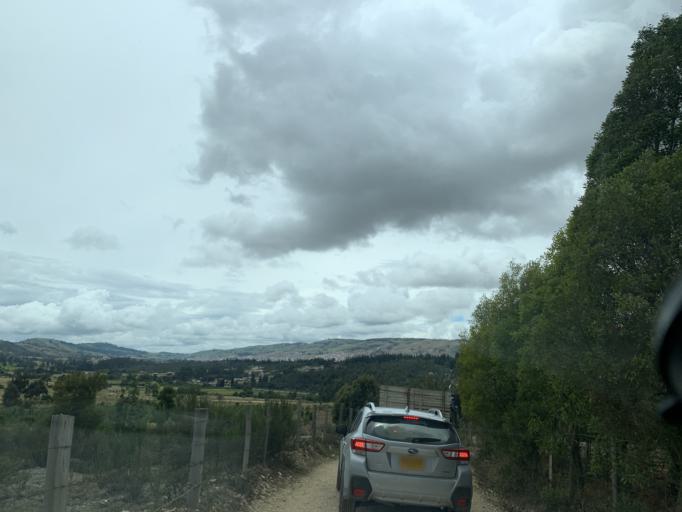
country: CO
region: Boyaca
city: Tunja
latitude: 5.5572
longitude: -73.3289
